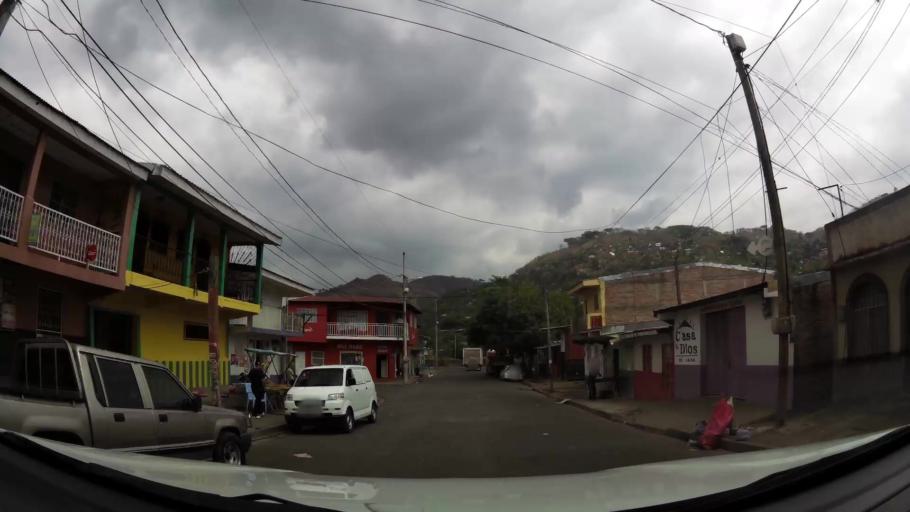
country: NI
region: Matagalpa
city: Matagalpa
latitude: 12.9223
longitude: -85.9235
